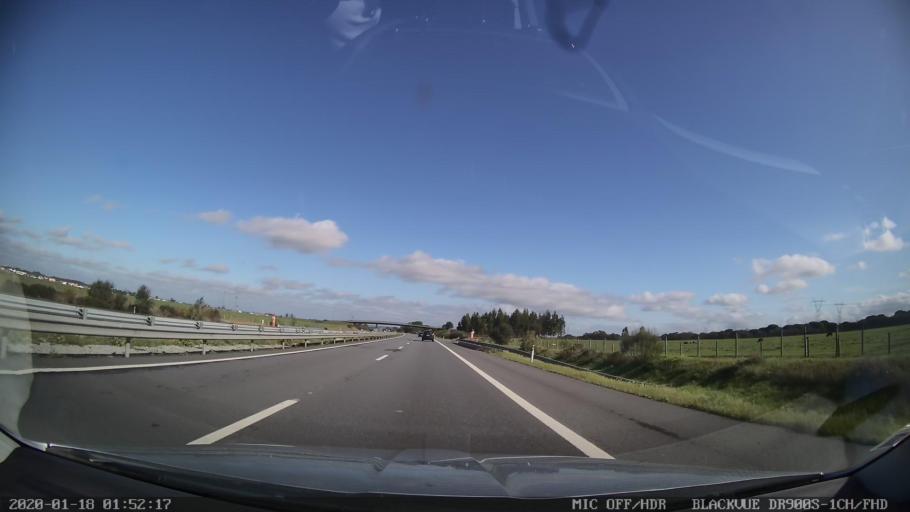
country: PT
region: Setubal
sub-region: Palmela
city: Palmela
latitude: 38.5936
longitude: -8.7498
